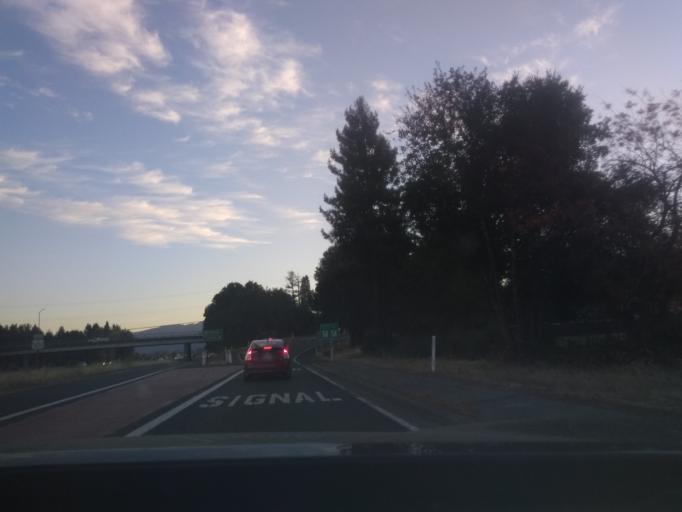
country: US
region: California
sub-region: Mendocino County
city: Ukiah
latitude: 39.1373
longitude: -123.1962
